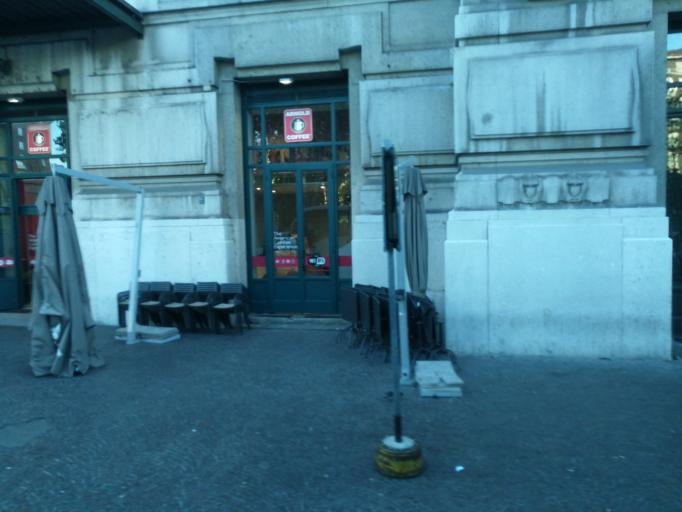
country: IT
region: Lombardy
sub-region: Citta metropolitana di Milano
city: Milano
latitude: 45.4859
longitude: 9.2058
